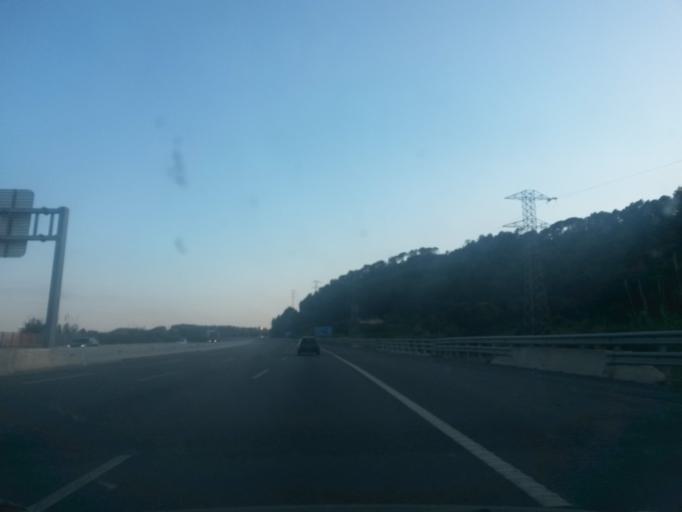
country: ES
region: Catalonia
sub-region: Provincia de Girona
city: Sarria de Ter
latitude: 42.0215
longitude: 2.8164
